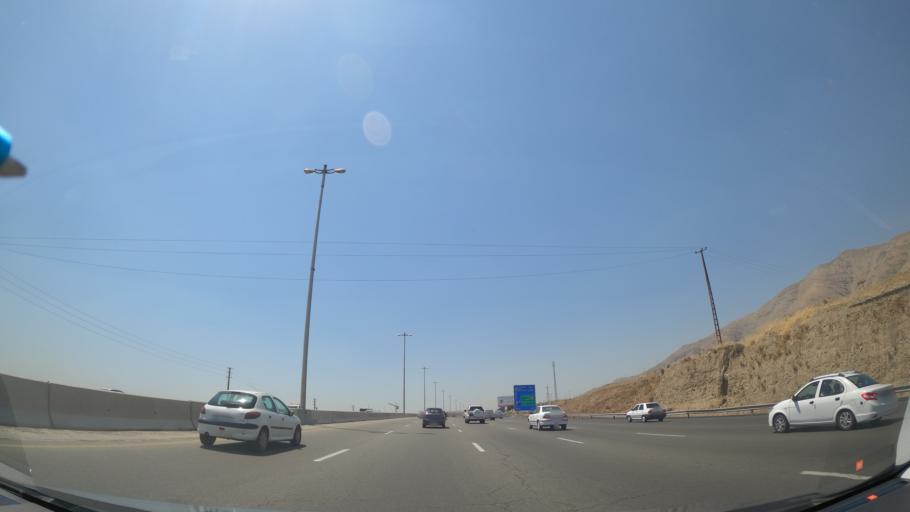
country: IR
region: Tehran
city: Shahr-e Qods
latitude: 35.7477
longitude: 51.0854
